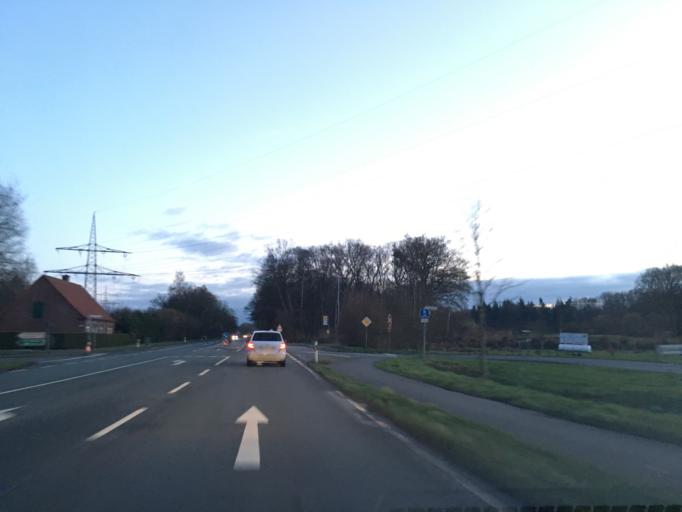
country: DE
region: North Rhine-Westphalia
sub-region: Regierungsbezirk Munster
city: Muenster
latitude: 51.8864
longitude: 7.6475
